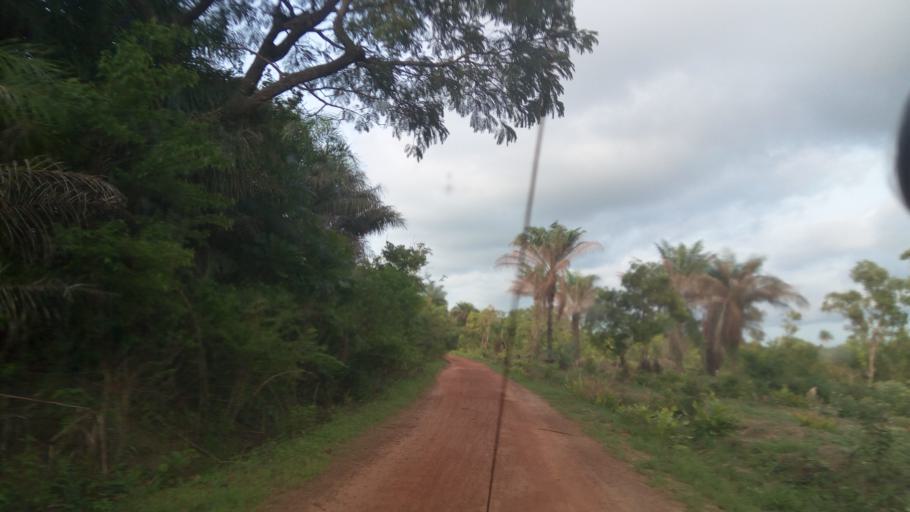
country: SL
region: Northern Province
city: Mambolo
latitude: 9.0248
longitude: -13.0270
